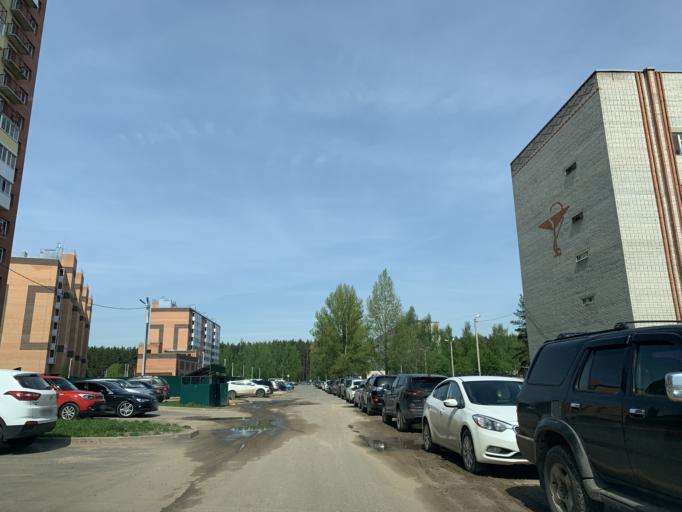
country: RU
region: Jaroslavl
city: Yaroslavl
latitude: 57.6548
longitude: 39.9682
